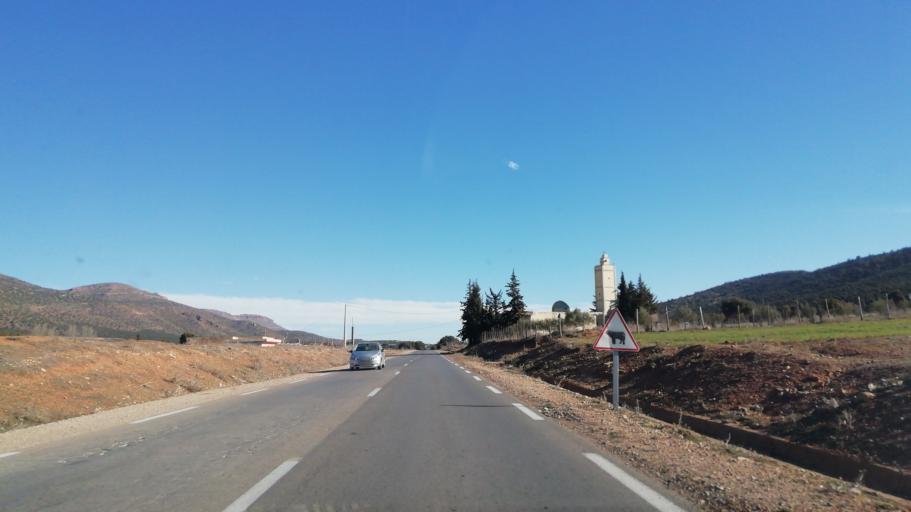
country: DZ
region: Tlemcen
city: Sebdou
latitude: 34.6894
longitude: -1.2442
